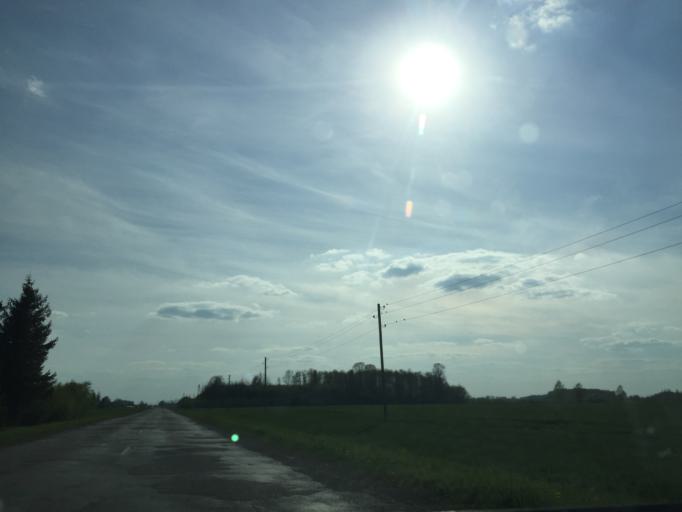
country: LV
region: Bauskas Rajons
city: Bauska
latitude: 56.4569
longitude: 24.2681
